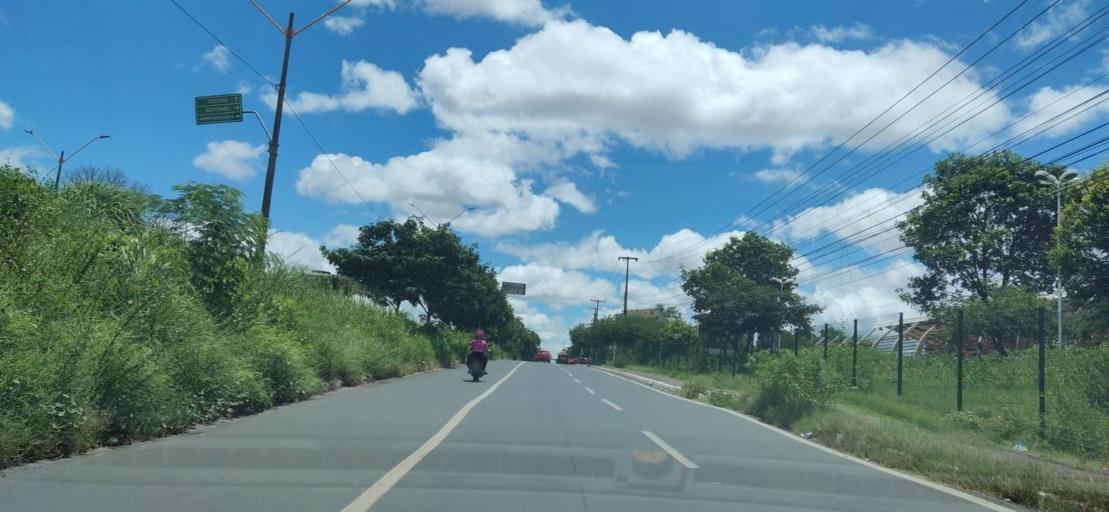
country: BR
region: Piaui
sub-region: Teresina
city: Teresina
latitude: -5.1433
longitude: -42.7785
